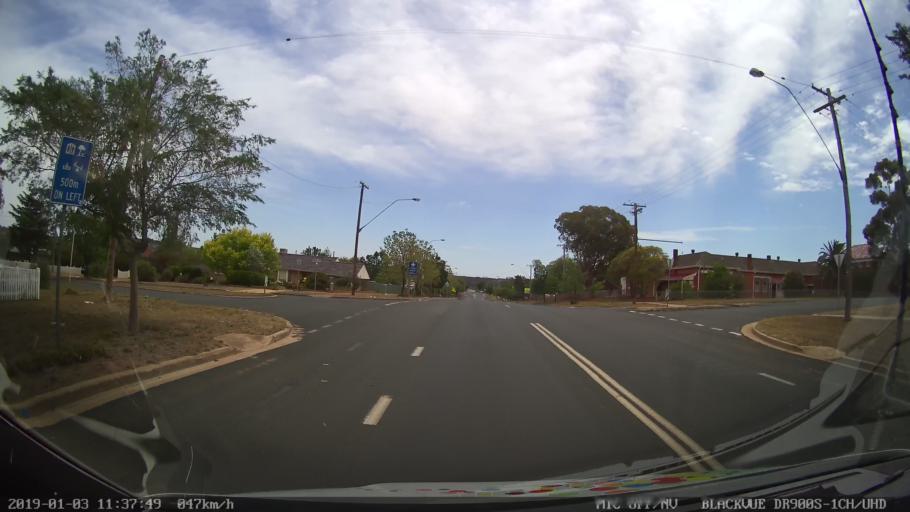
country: AU
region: New South Wales
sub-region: Weddin
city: Grenfell
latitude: -33.9004
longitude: 148.1617
